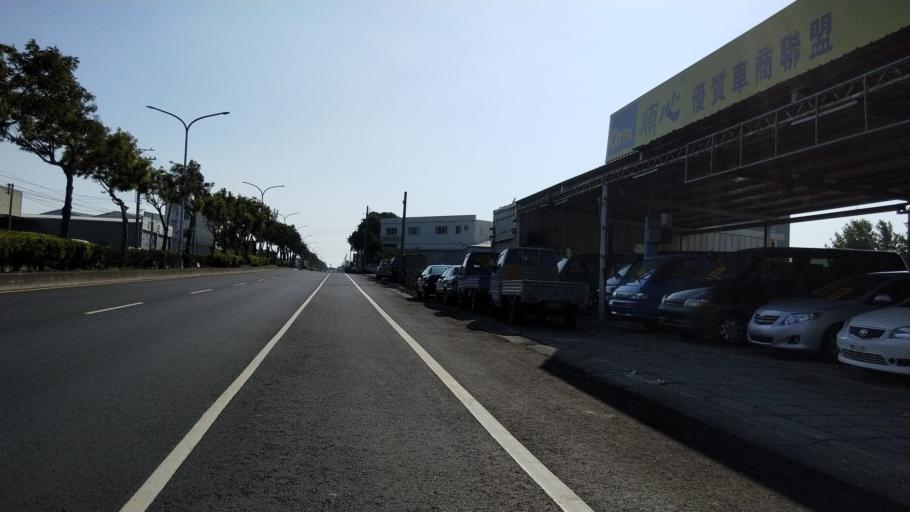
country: TW
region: Taiwan
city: Fengyuan
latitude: 24.3323
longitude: 120.6133
